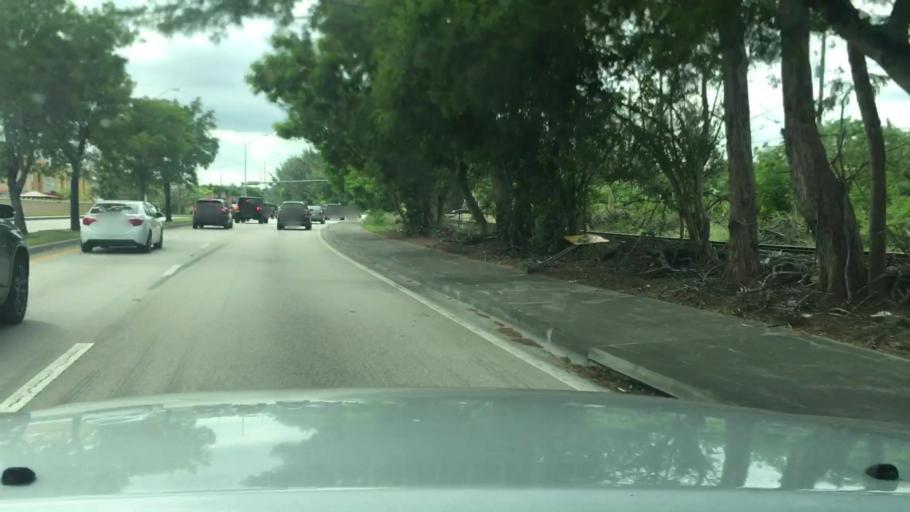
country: US
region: Florida
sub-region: Miami-Dade County
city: Tamiami
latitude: 25.7823
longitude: -80.3991
